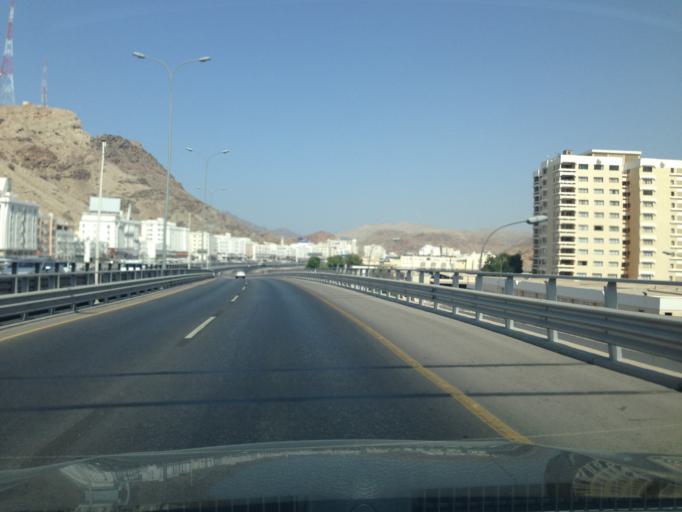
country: OM
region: Muhafazat Masqat
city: Muscat
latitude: 23.5915
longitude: 58.5260
